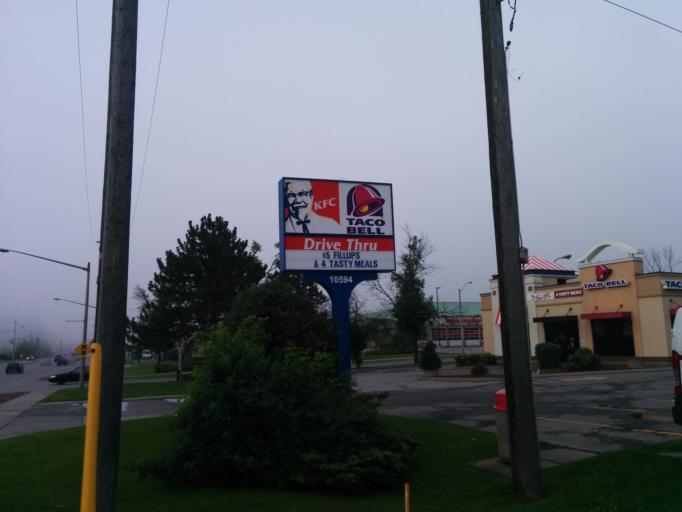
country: CA
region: Ontario
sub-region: York
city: Richmond Hill
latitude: 43.8859
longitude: -79.4408
